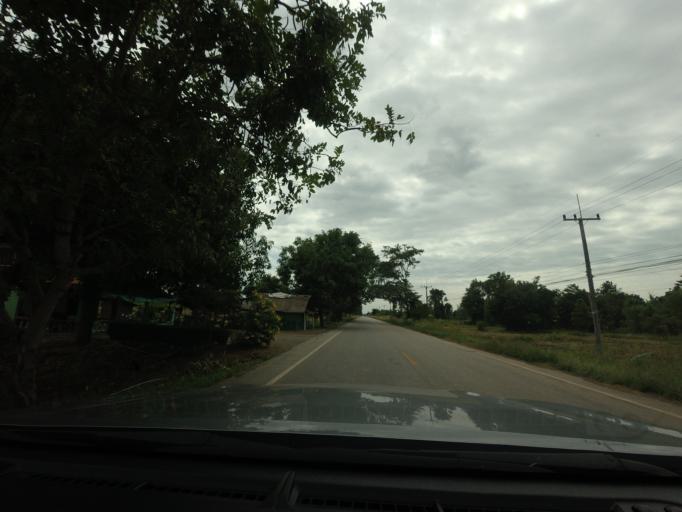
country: TH
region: Phitsanulok
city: Noen Maprang
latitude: 16.6515
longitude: 100.6162
